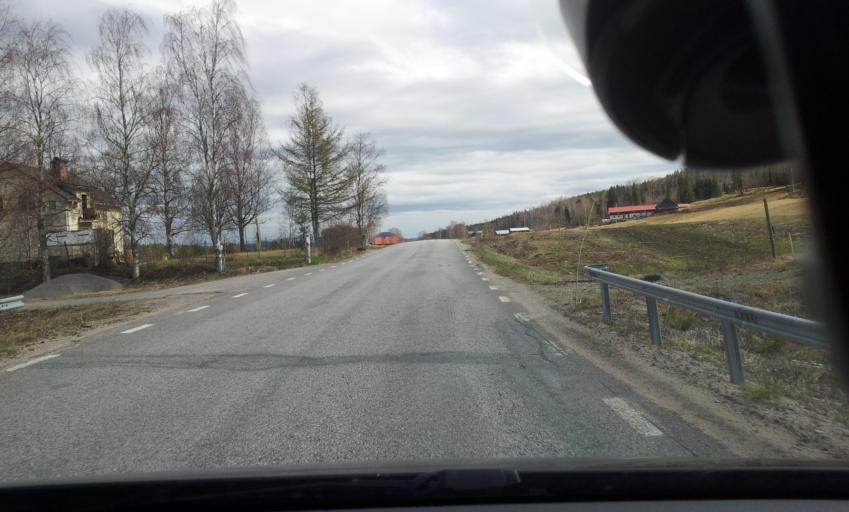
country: SE
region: Gaevleborg
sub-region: Ljusdals Kommun
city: Ljusdal
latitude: 61.7672
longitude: 16.0373
